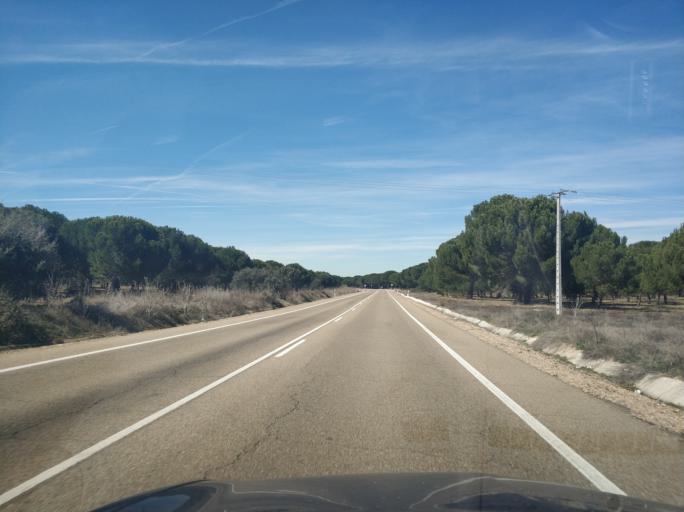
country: ES
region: Castille and Leon
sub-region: Provincia de Valladolid
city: Viana de Cega
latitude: 41.5379
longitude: -4.7668
